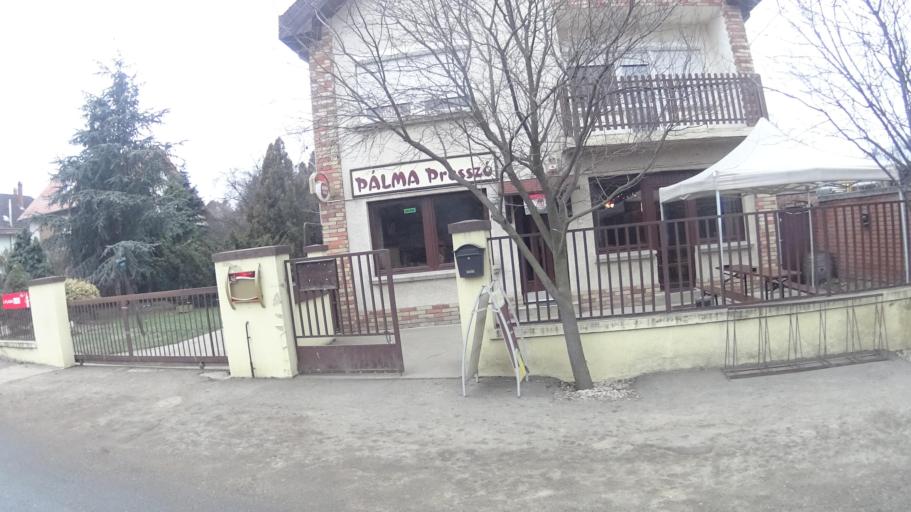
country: HU
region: Pest
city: Kosd
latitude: 47.8065
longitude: 19.1772
